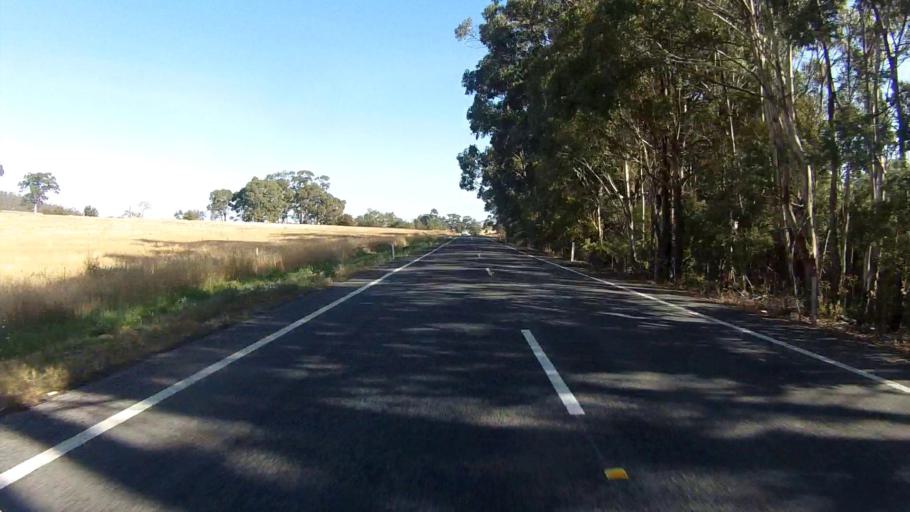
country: AU
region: Tasmania
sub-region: Sorell
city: Sorell
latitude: -42.6964
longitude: 147.5258
